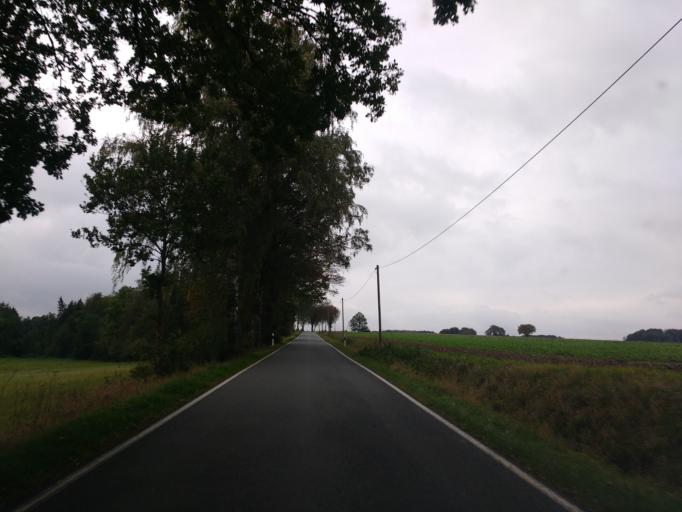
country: DE
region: North Rhine-Westphalia
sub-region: Regierungsbezirk Detmold
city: Lemgo
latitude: 51.9765
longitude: 8.9554
